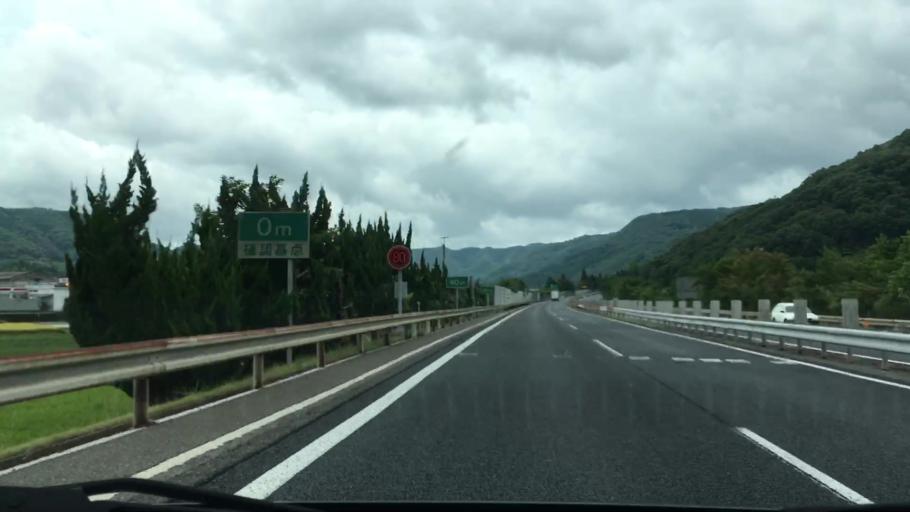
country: JP
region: Okayama
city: Niimi
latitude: 34.9707
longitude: 133.6502
